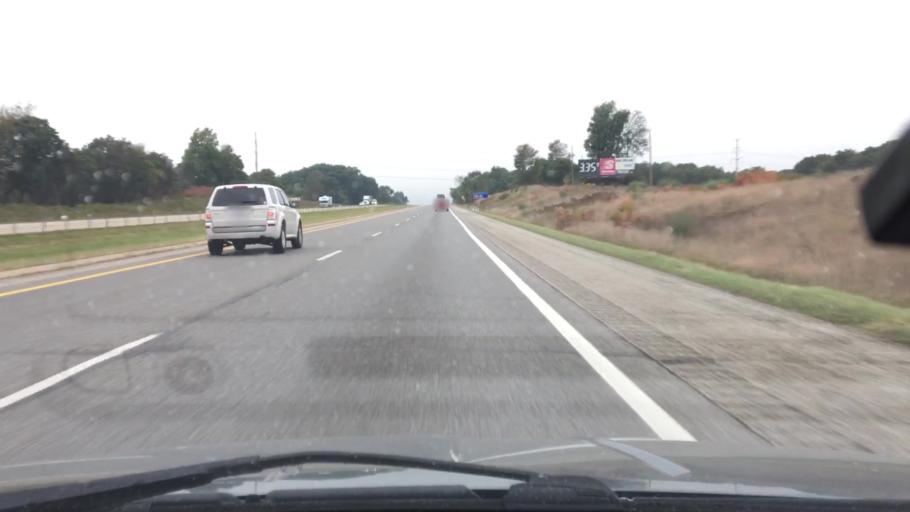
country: US
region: Michigan
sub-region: Van Buren County
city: Mattawan
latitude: 42.2233
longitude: -85.7591
